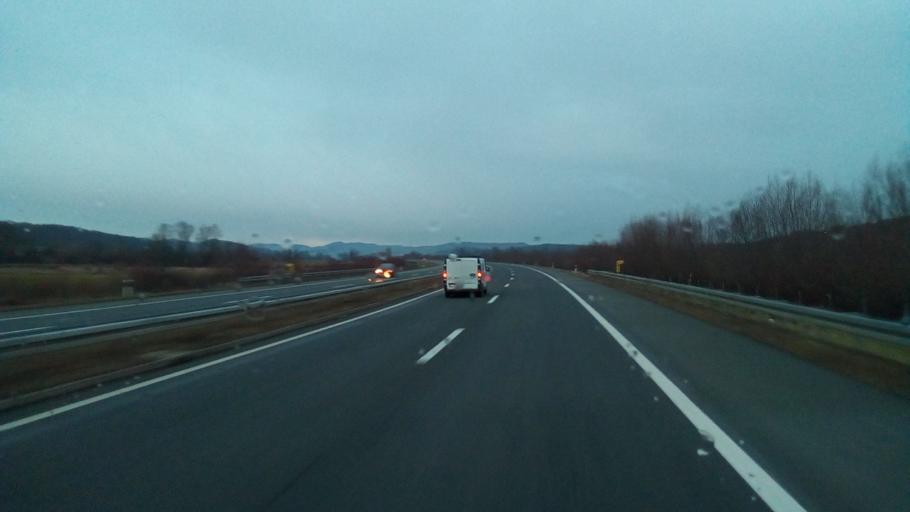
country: HR
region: Zagrebacka
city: Brckovljani
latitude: 46.0069
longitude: 16.2941
